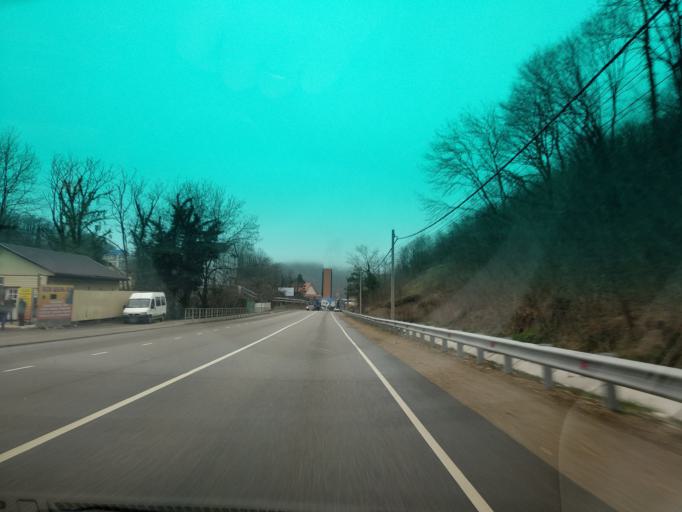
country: RU
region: Krasnodarskiy
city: Tuapse
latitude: 44.1107
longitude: 39.0726
